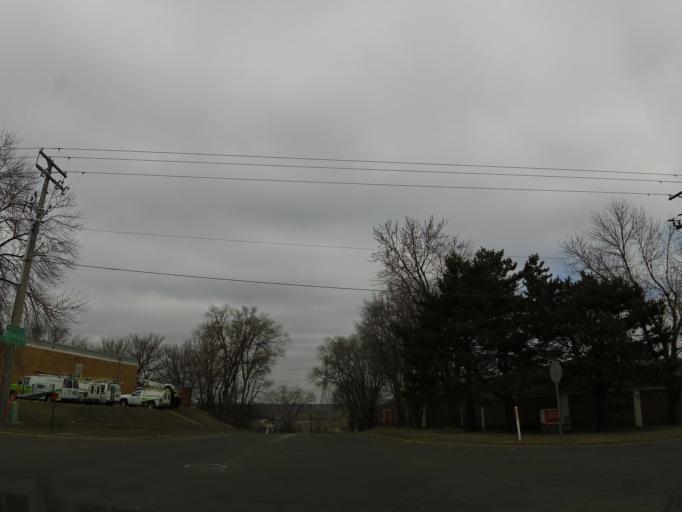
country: US
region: Minnesota
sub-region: Dakota County
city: Burnsville
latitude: 44.7718
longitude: -93.3073
